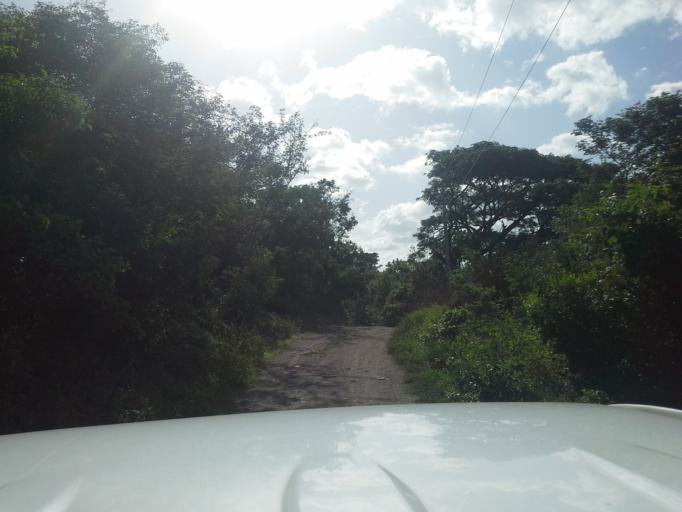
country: NI
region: Matagalpa
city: Ciudad Dario
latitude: 12.6687
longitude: -86.0463
